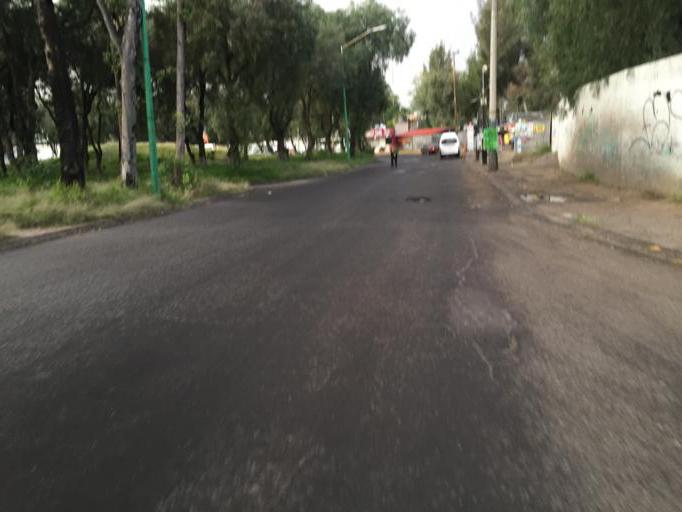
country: MX
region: Mexico
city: Cuautitlan Izcalli
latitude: 19.6723
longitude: -99.2144
